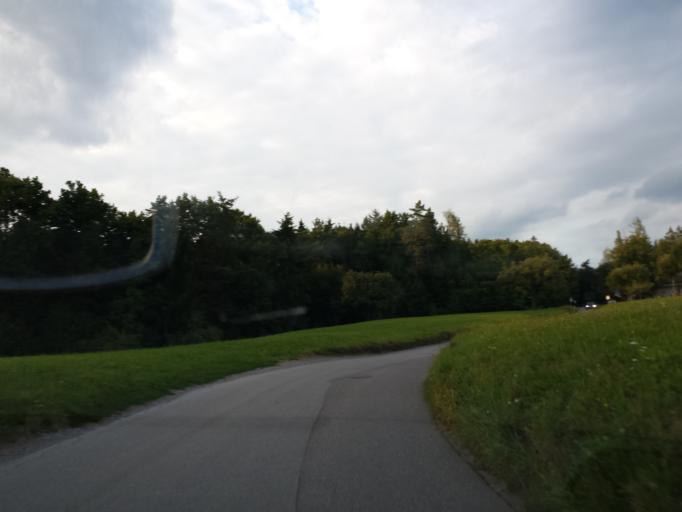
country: AT
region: Styria
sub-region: Politischer Bezirk Graz-Umgebung
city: Stattegg
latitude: 47.1307
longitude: 15.4385
